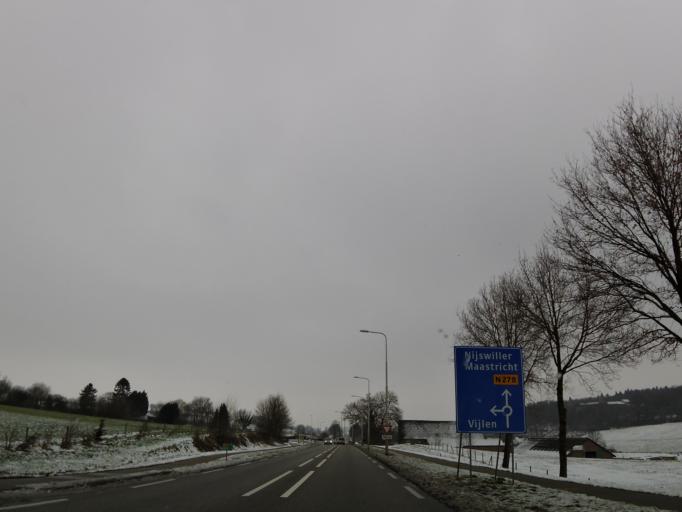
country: NL
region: Limburg
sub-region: Gemeente Simpelveld
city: Simpelveld
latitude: 50.7960
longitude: 5.9753
